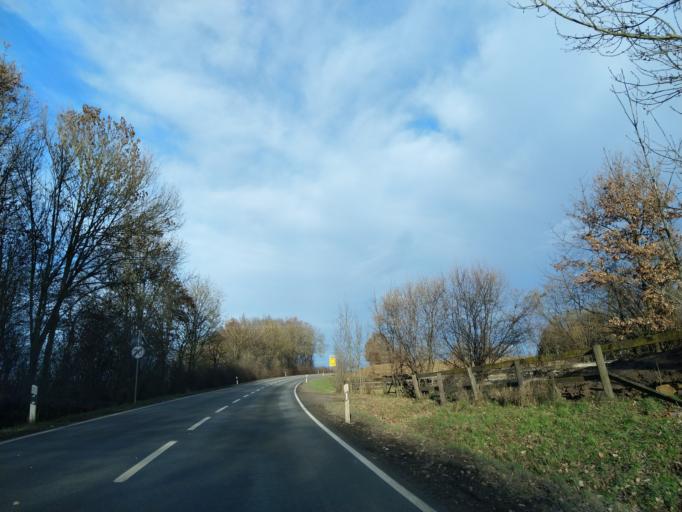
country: DE
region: Bavaria
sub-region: Lower Bavaria
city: Kunzing
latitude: 48.6509
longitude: 13.0456
